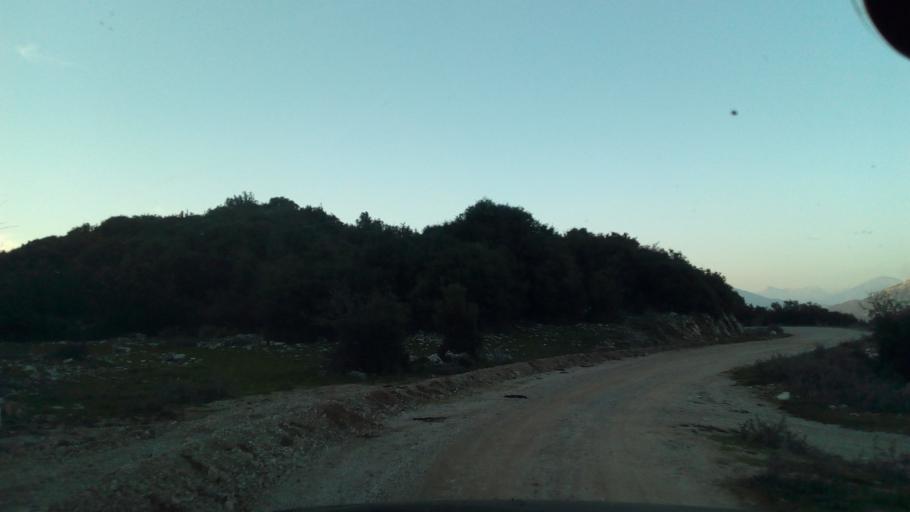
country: GR
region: West Greece
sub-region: Nomos Aitolias kai Akarnanias
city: Nafpaktos
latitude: 38.4664
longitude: 21.8254
